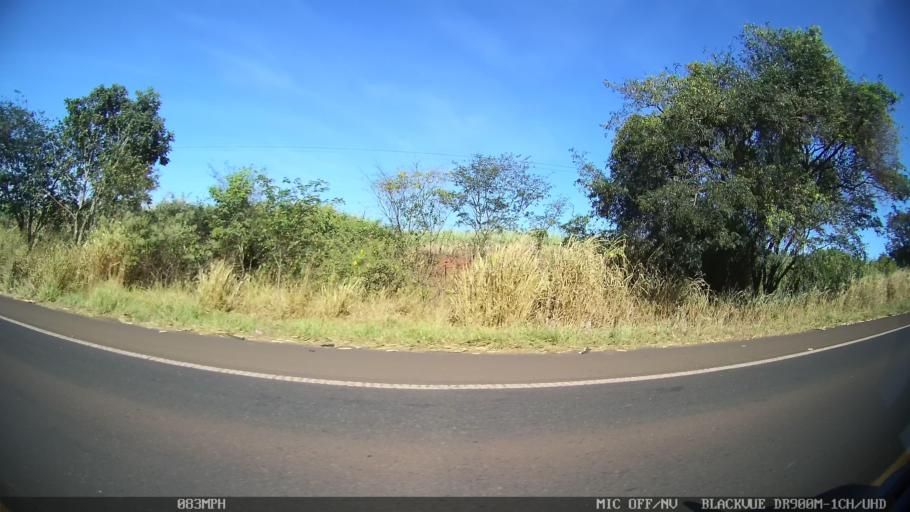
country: BR
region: Sao Paulo
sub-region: Barretos
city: Barretos
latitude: -20.5505
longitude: -48.6331
